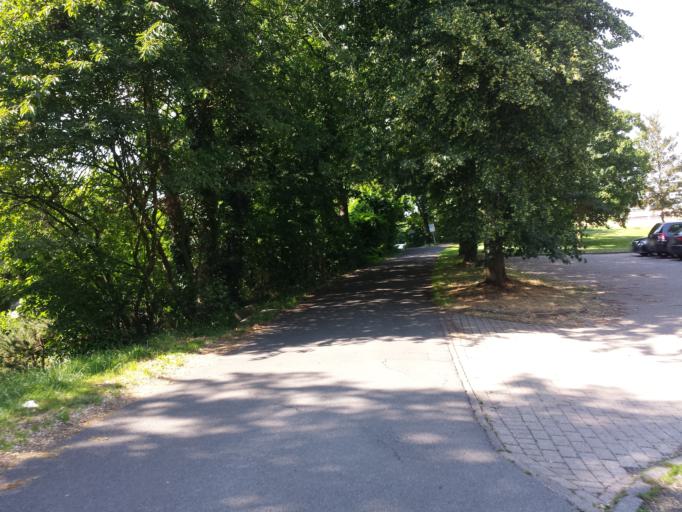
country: DE
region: Bremen
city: Bremen
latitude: 53.0913
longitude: 8.7613
